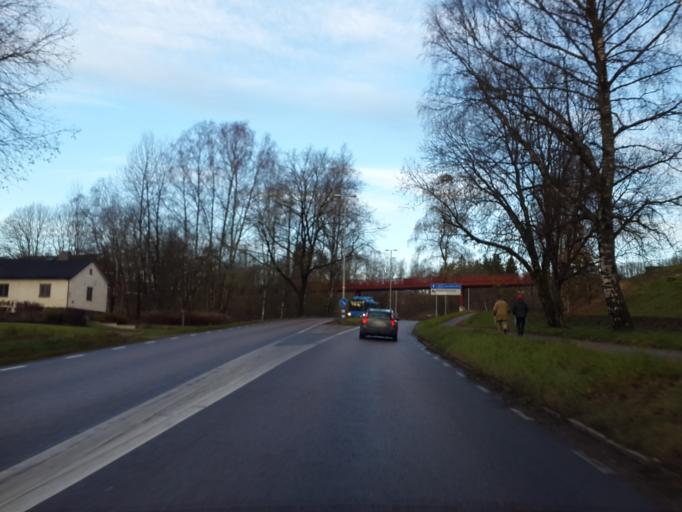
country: SE
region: Vaestra Goetaland
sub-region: Boras Kommun
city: Boras
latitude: 57.7279
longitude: 12.9085
